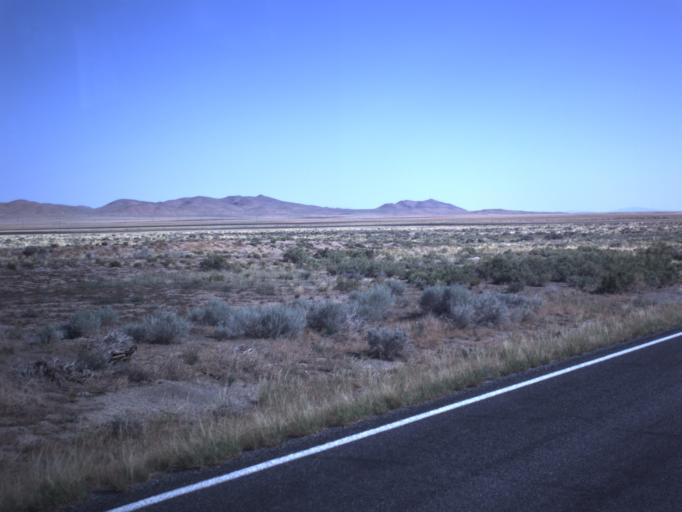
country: US
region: Utah
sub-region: Millard County
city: Delta
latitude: 38.9586
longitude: -112.8040
